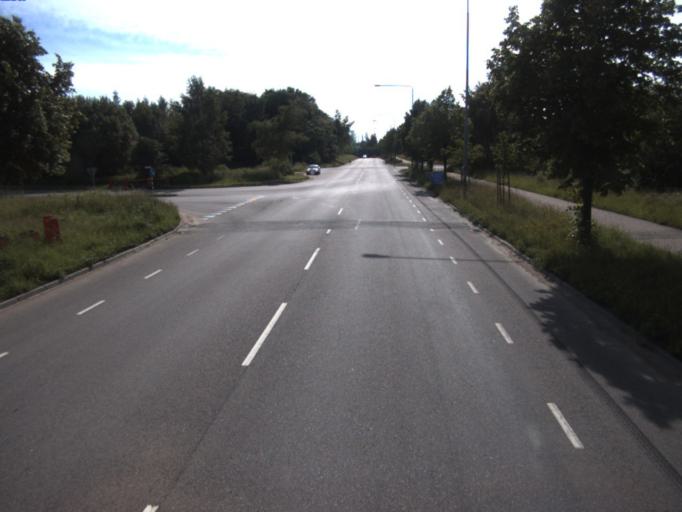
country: SE
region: Skane
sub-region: Helsingborg
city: Odakra
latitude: 56.0750
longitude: 12.7452
